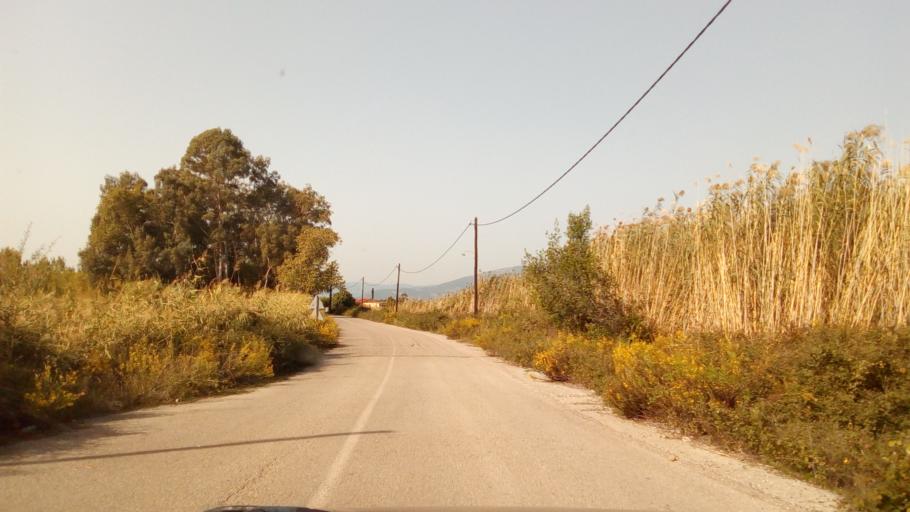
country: GR
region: West Greece
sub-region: Nomos Aitolias kai Akarnanias
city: Nafpaktos
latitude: 38.4032
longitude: 21.9252
